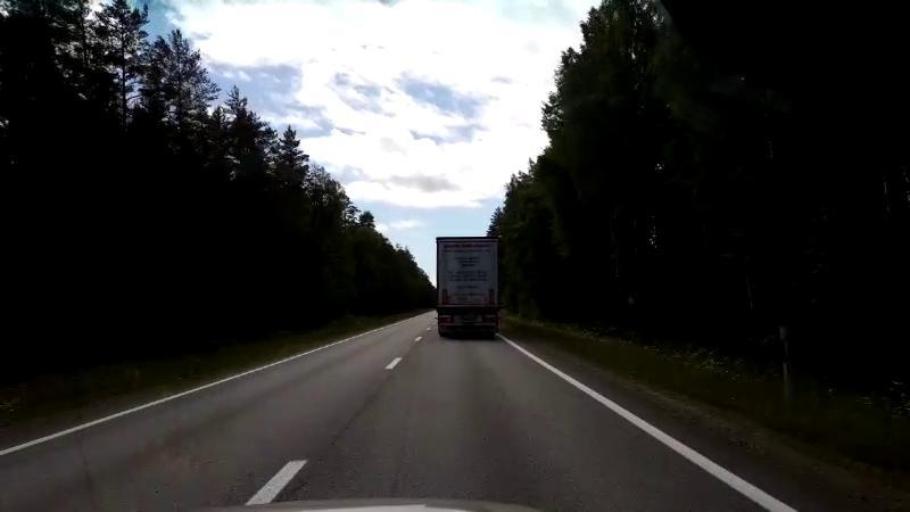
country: LV
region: Salacgrivas
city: Salacgriva
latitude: 57.5225
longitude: 24.4308
